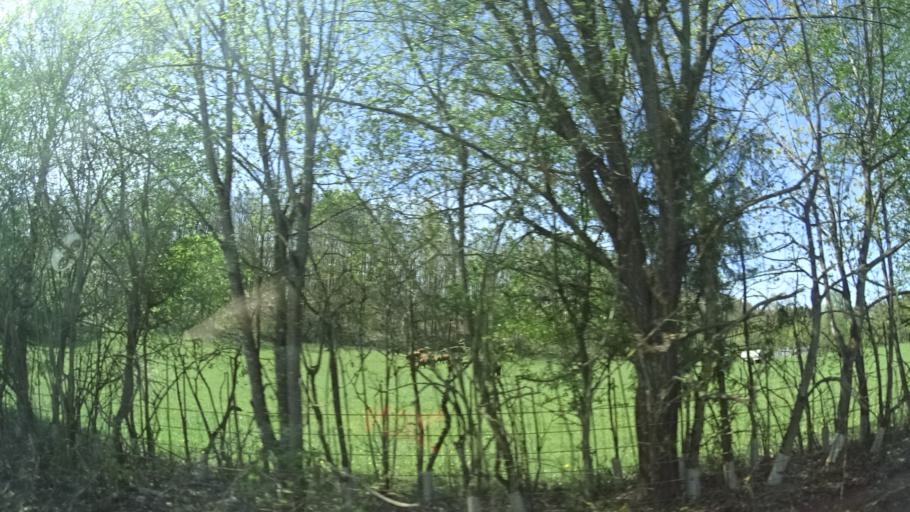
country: DE
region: Bavaria
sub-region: Upper Franconia
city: Weitramsdorf
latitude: 50.2981
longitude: 10.7921
